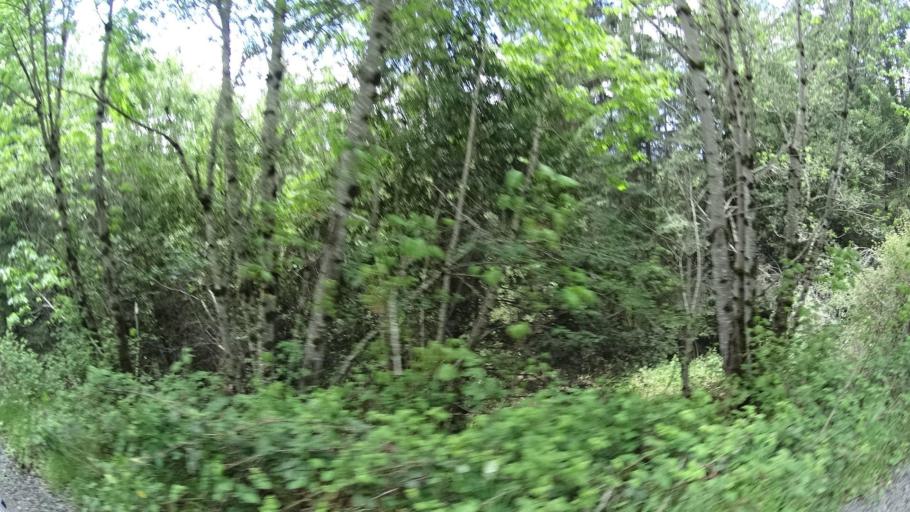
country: US
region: California
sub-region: Humboldt County
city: Blue Lake
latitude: 40.8127
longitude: -123.8867
